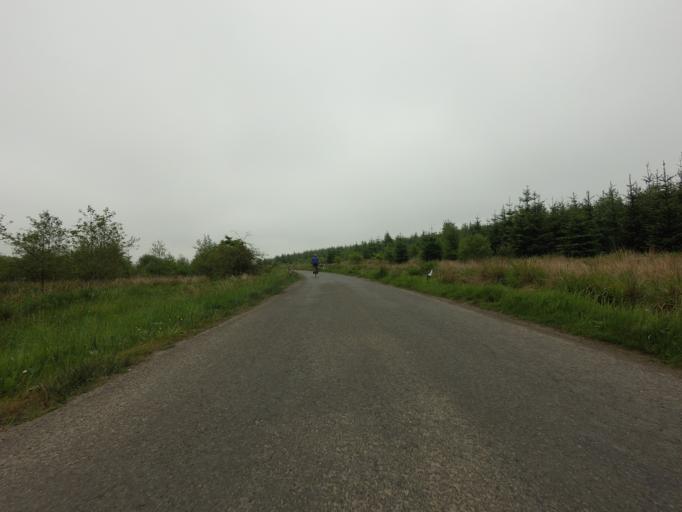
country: GB
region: Scotland
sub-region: Fife
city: Townhill
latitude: 56.1292
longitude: -3.4410
